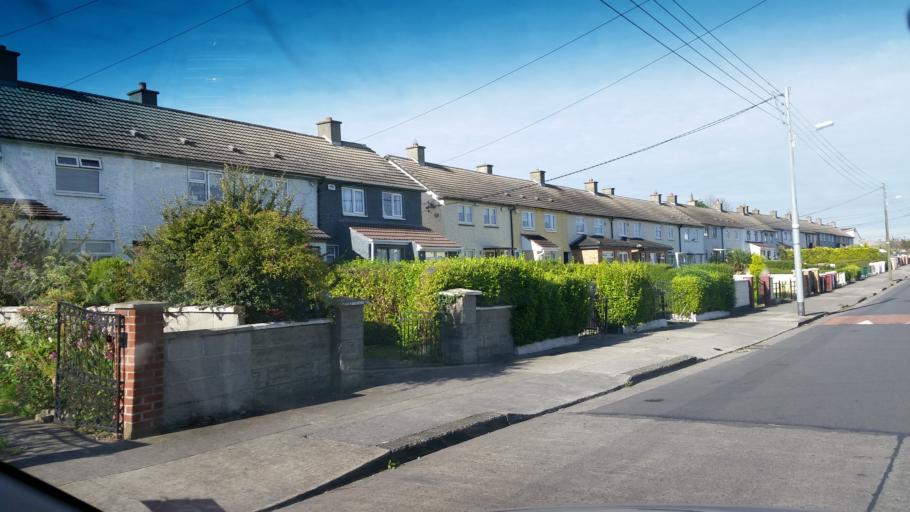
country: IE
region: Leinster
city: Beaumont
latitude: 53.3934
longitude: -6.2268
